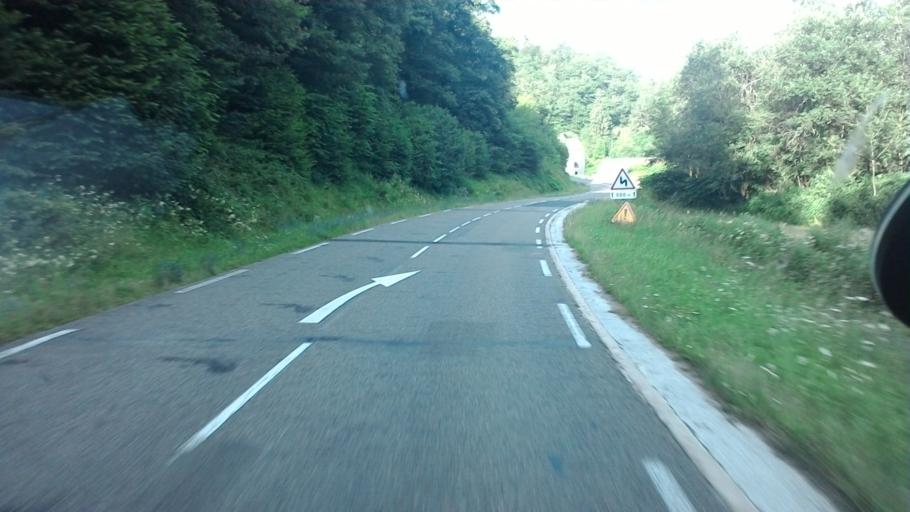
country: FR
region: Lorraine
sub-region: Departement des Vosges
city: Rupt-sur-Moselle
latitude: 47.8880
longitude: 6.6114
